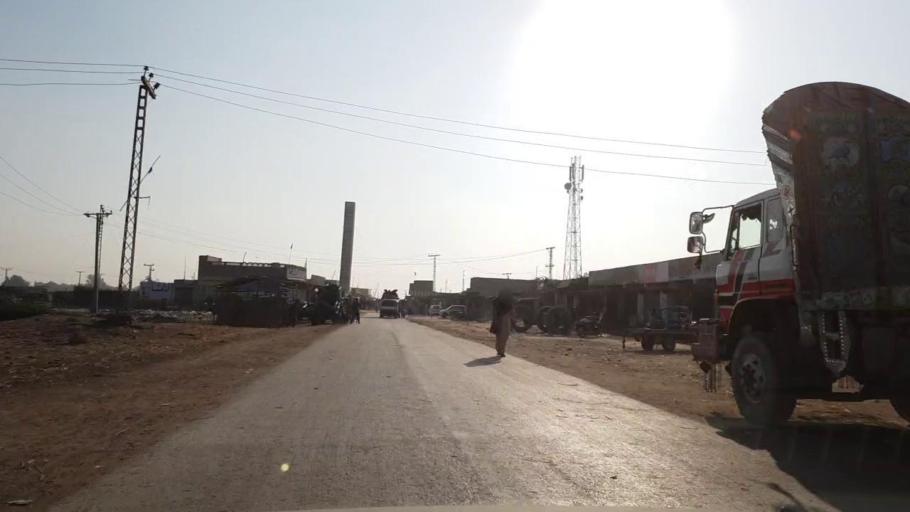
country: PK
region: Sindh
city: Bulri
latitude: 24.8121
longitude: 68.3198
